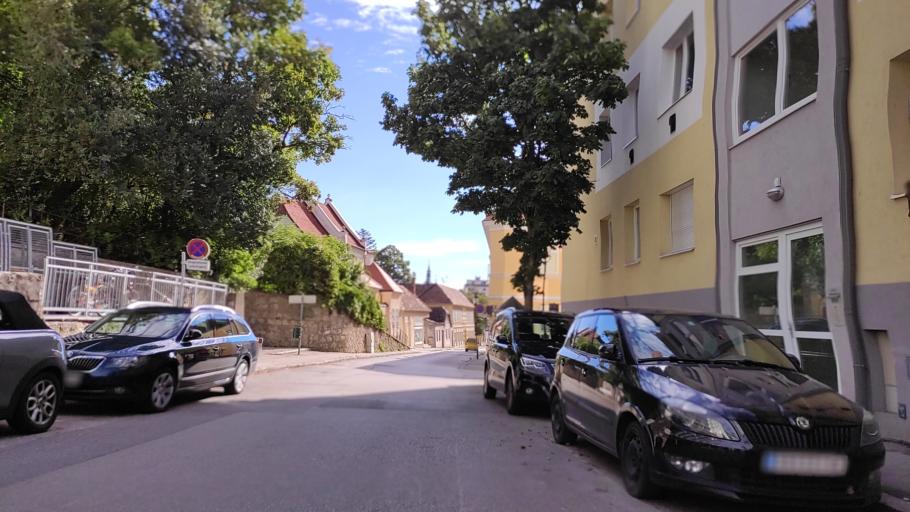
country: AT
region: Lower Austria
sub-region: Politischer Bezirk Baden
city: Baden
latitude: 48.0096
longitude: 16.2277
